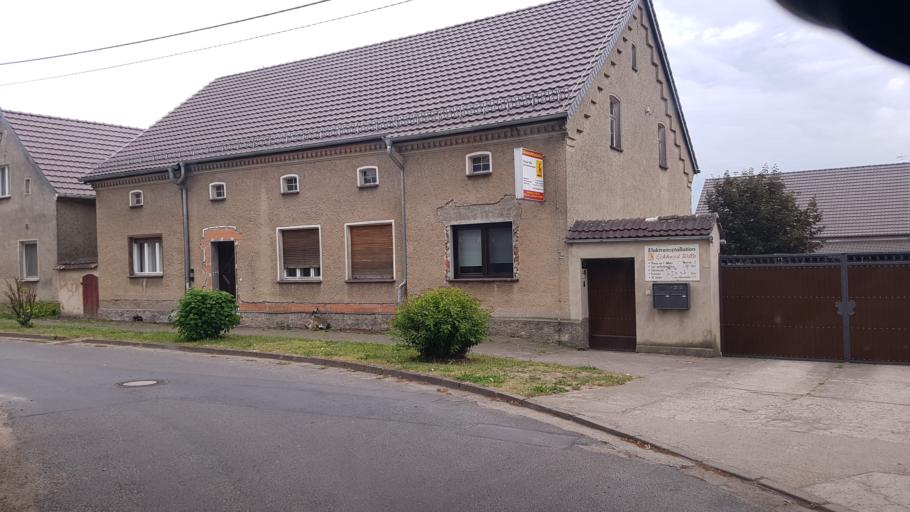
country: DE
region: Brandenburg
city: Herzberg
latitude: 51.7606
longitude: 13.2571
